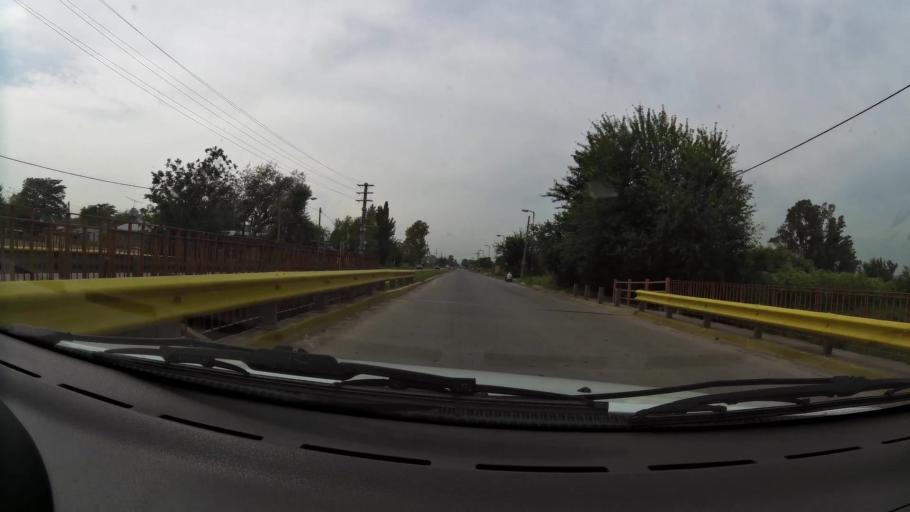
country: AR
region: Buenos Aires
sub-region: Partido de La Plata
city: La Plata
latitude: -34.9279
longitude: -58.0156
